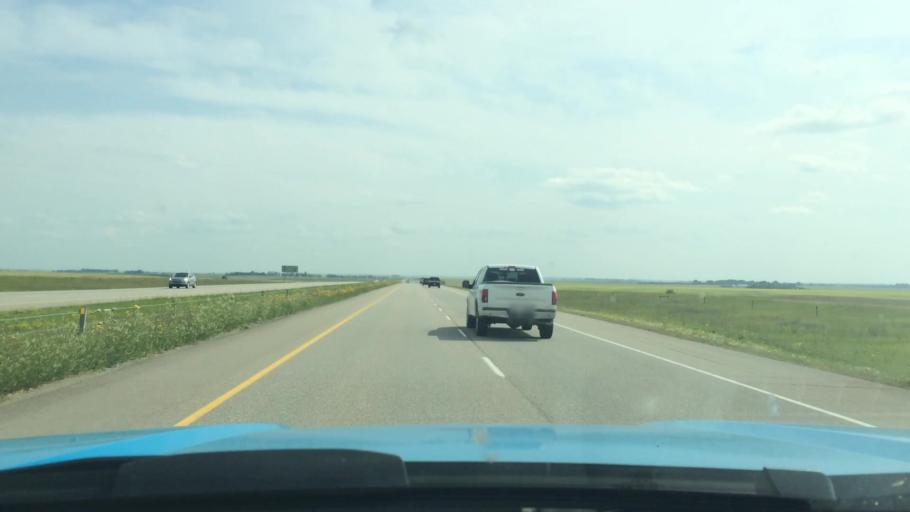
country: CA
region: Alberta
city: Didsbury
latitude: 51.6496
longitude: -114.0256
